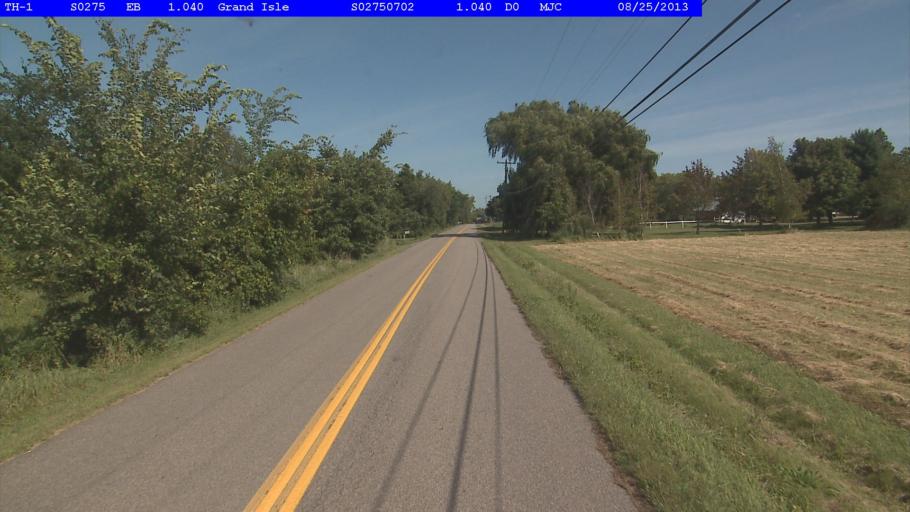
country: US
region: New York
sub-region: Clinton County
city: Cumberland Head
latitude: 44.7153
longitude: -73.3418
